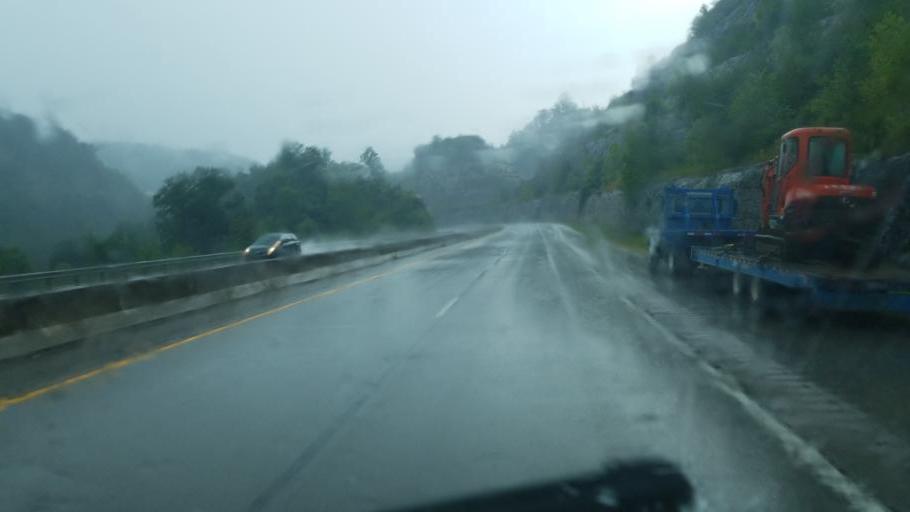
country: US
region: West Virginia
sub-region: Mingo County
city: Williamson
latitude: 37.6159
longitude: -82.3438
